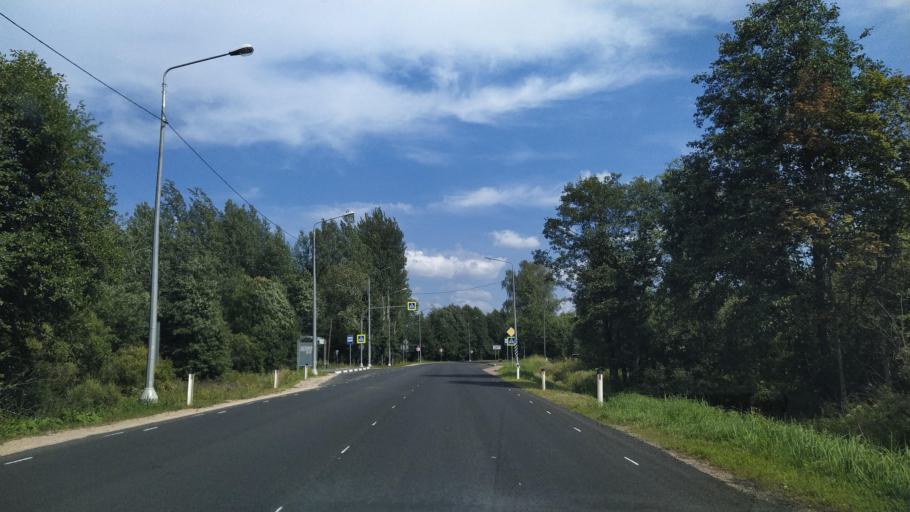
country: RU
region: Pskov
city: Porkhov
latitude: 57.7438
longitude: 29.0439
